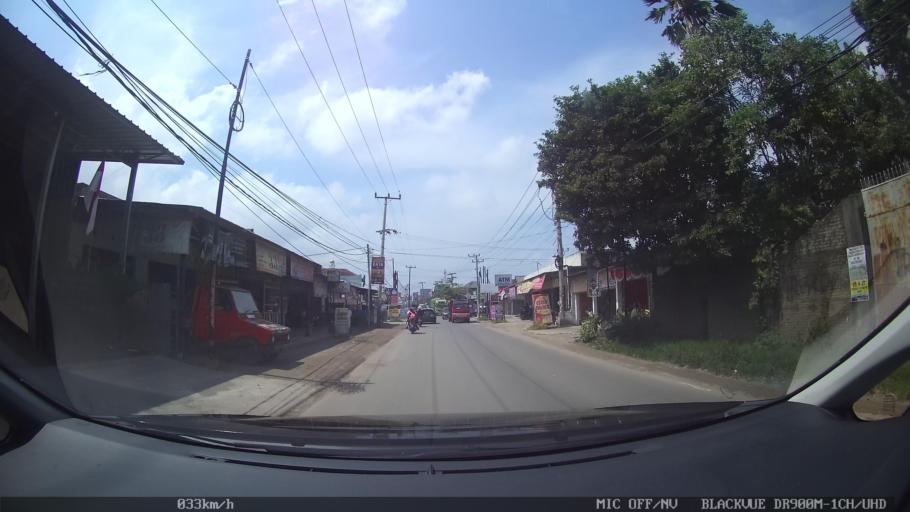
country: ID
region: Lampung
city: Kedaton
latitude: -5.3524
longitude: 105.2996
